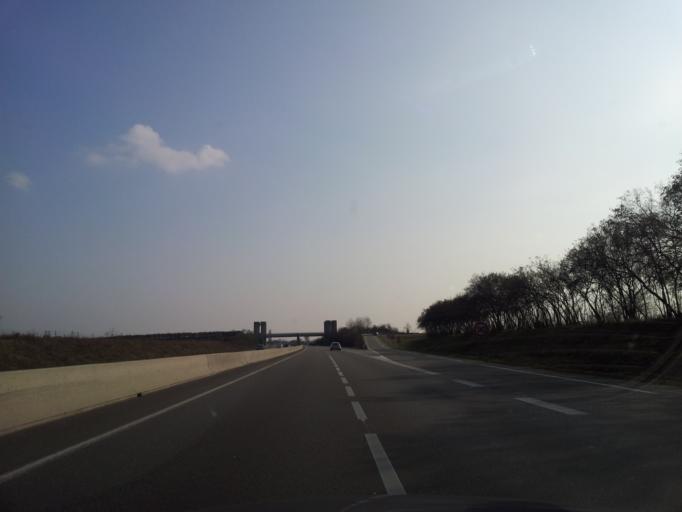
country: FR
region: Alsace
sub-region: Departement du Haut-Rhin
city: Meyenheim
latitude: 47.9271
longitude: 7.3596
